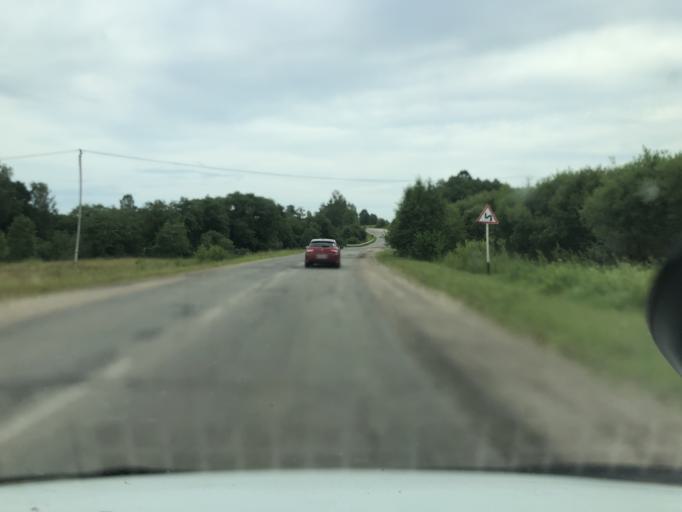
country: RU
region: Jaroslavl
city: Petrovsk
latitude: 56.9849
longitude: 39.1366
